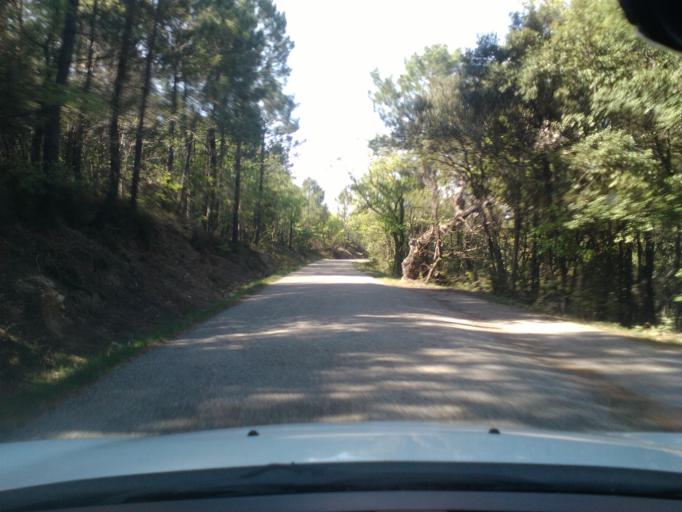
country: FR
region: Languedoc-Roussillon
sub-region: Departement du Gard
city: Lasalle
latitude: 44.0137
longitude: 3.8783
